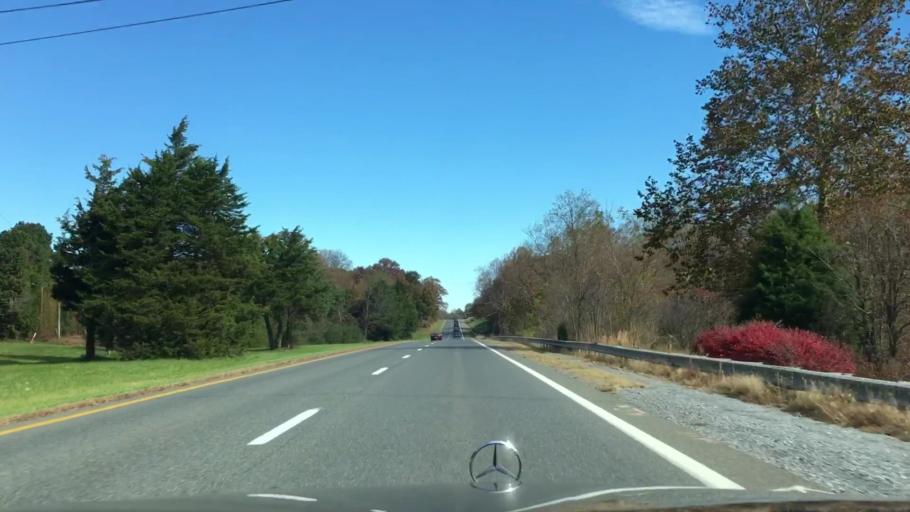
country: US
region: Virginia
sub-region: Campbell County
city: Altavista
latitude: 37.1598
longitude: -79.2221
